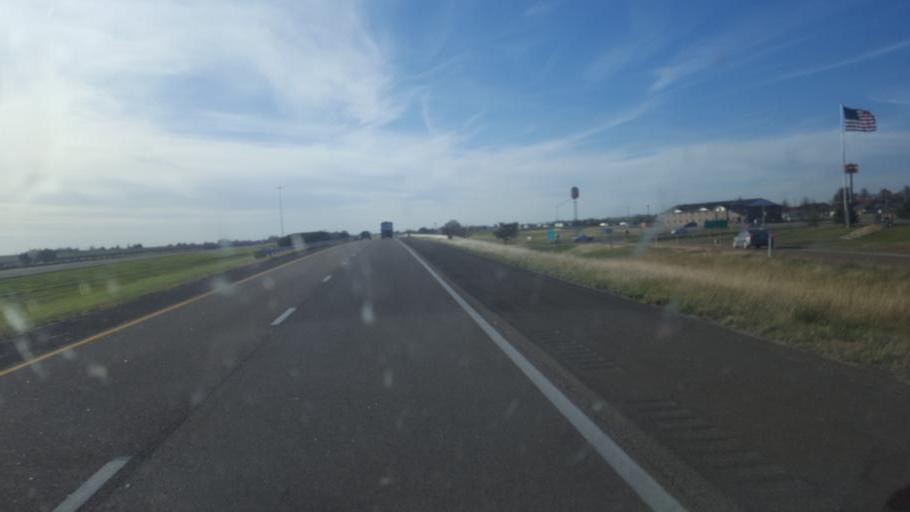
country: US
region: Kansas
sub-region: Trego County
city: WaKeeney
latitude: 39.0106
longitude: -99.8694
